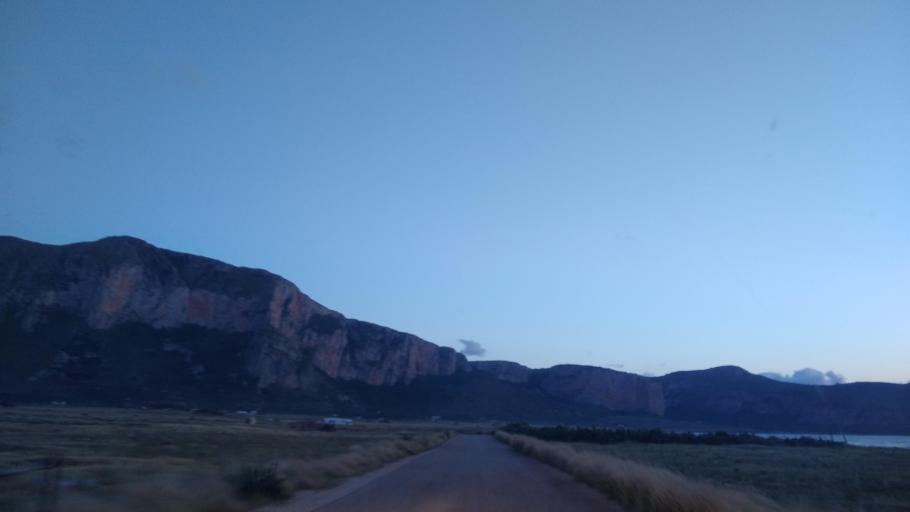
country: IT
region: Sicily
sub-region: Trapani
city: Castelluzzo
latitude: 38.1191
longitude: 12.7223
